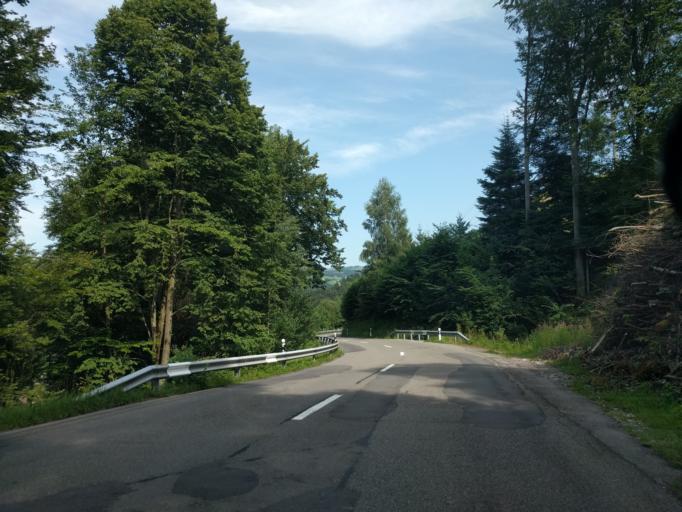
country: CH
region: Saint Gallen
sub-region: Wahlkreis Toggenburg
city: Oberhelfenschwil
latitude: 47.3275
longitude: 9.1233
